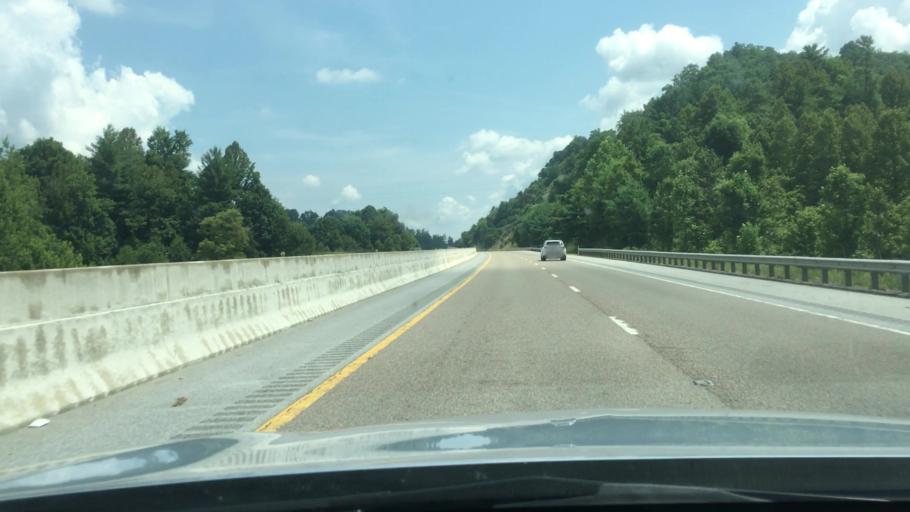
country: US
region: Tennessee
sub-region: Unicoi County
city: Banner Hill
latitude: 36.0366
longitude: -82.5342
